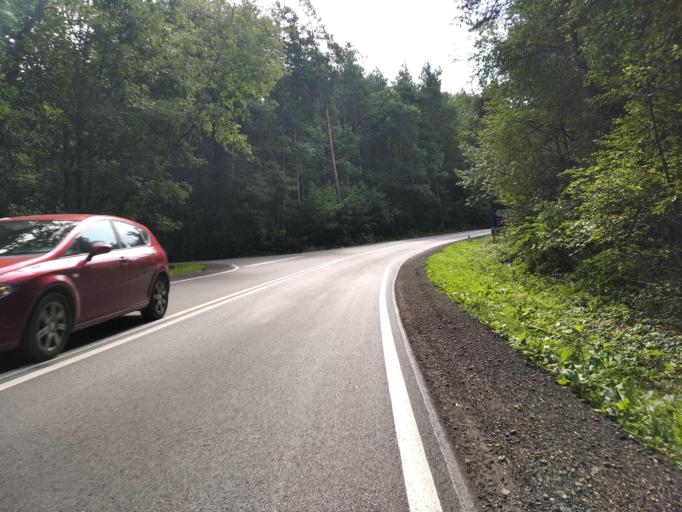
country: PL
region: Subcarpathian Voivodeship
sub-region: Powiat ropczycko-sedziszowski
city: Ostrow
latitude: 50.1313
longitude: 21.5881
